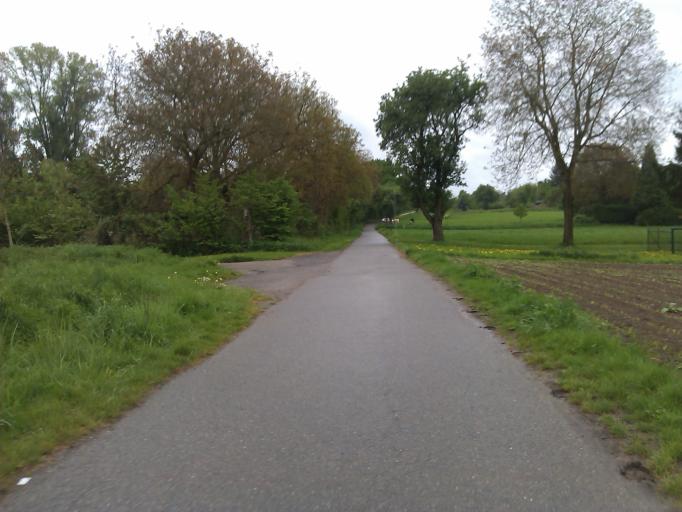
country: DE
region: Baden-Wuerttemberg
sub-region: Karlsruhe Region
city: Ettlingen
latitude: 48.9556
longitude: 8.4181
